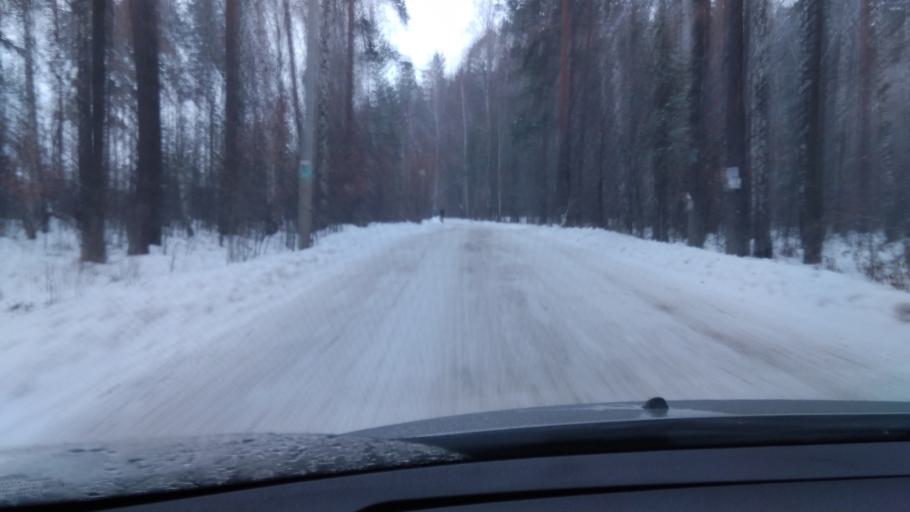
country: RU
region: Sverdlovsk
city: Verkhnyaya Pyshma
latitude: 56.9232
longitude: 60.5858
